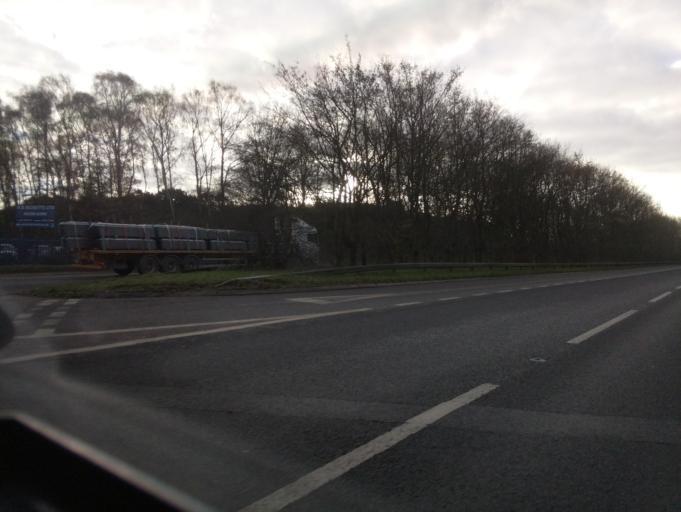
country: GB
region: England
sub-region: Staffordshire
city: Shenstone
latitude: 52.6198
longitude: -1.7985
